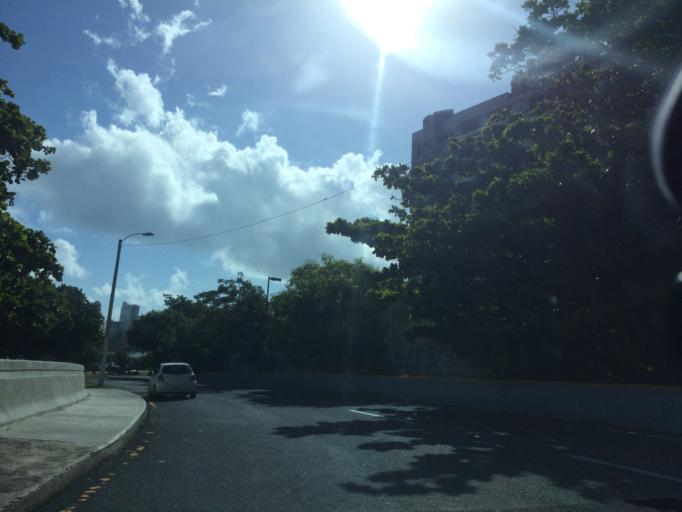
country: PR
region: San Juan
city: San Juan
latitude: 18.4576
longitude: -66.0861
